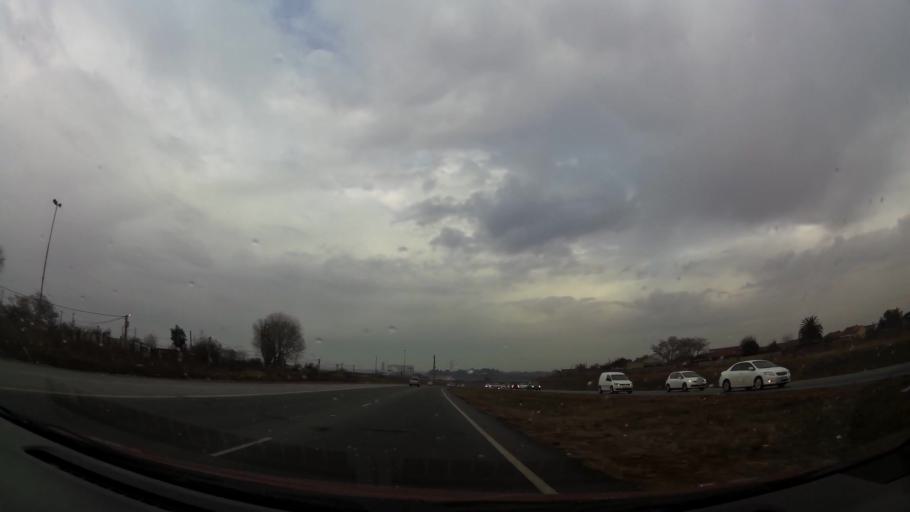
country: ZA
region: Gauteng
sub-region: City of Johannesburg Metropolitan Municipality
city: Soweto
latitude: -26.3050
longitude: 27.8948
